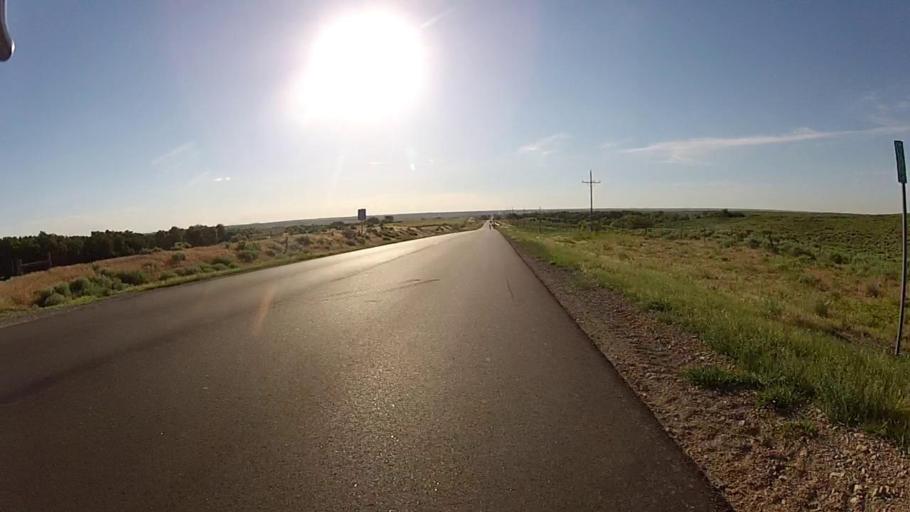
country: US
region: Kansas
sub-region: Comanche County
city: Coldwater
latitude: 37.2820
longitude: -99.0915
